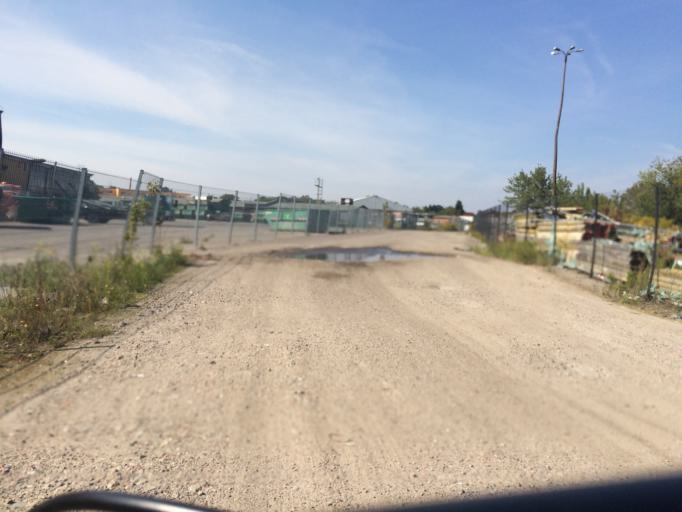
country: DE
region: Berlin
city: Heinersdorf
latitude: 52.5731
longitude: 13.4489
